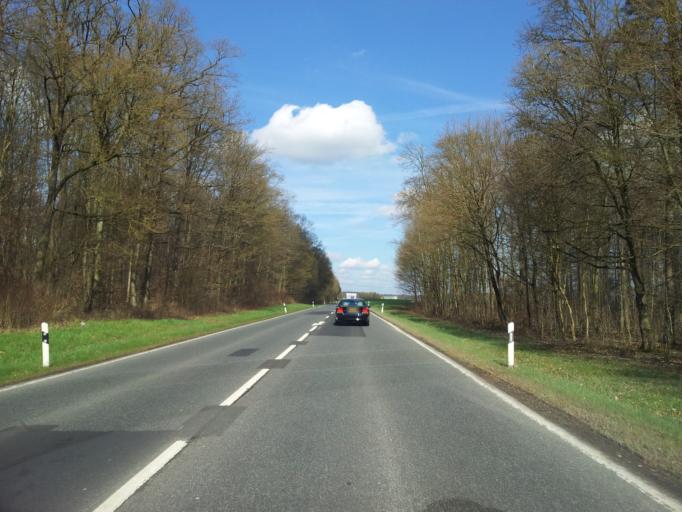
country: DE
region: Bavaria
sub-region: Regierungsbezirk Unterfranken
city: Kist
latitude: 49.7300
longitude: 9.8327
